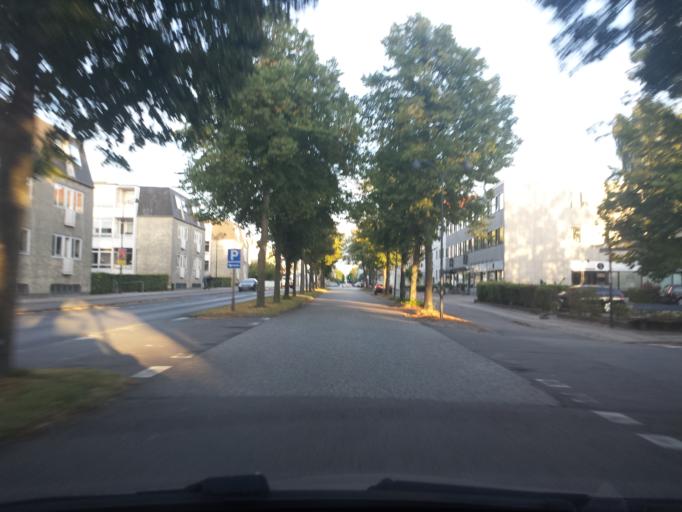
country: DK
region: Capital Region
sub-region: Gentofte Kommune
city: Charlottenlund
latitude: 55.7560
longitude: 12.5645
